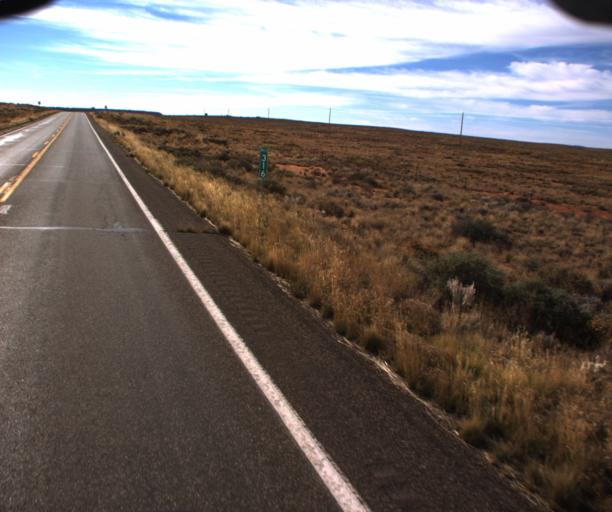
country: US
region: Arizona
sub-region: Coconino County
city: Kaibito
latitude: 36.7086
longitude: -111.2699
